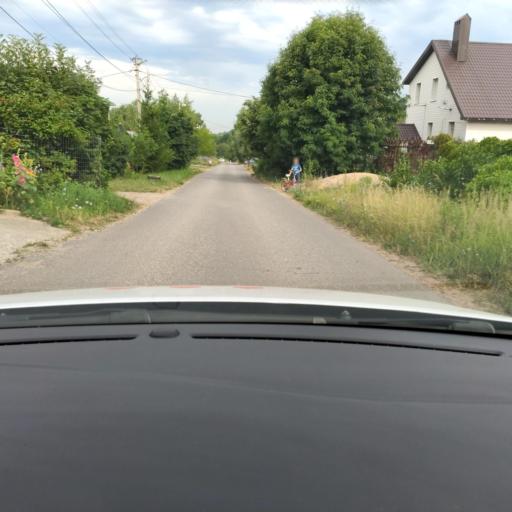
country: RU
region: Tatarstan
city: Stolbishchi
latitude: 55.7586
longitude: 49.2861
